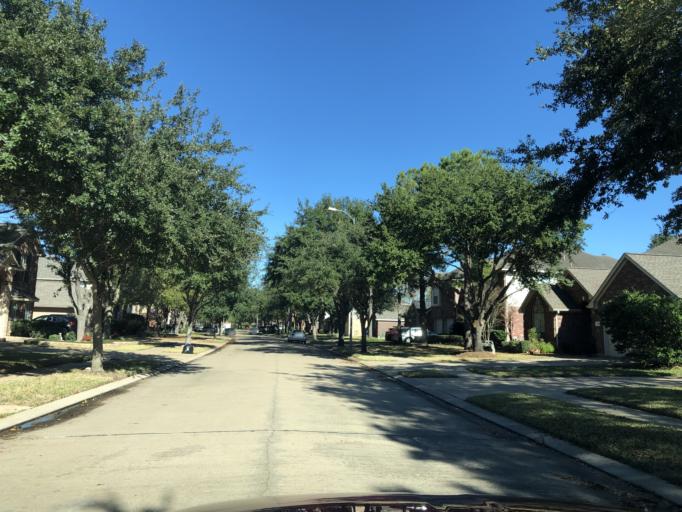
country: US
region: Texas
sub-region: Harris County
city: Oak Cliff Place
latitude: 29.9344
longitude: -95.6611
